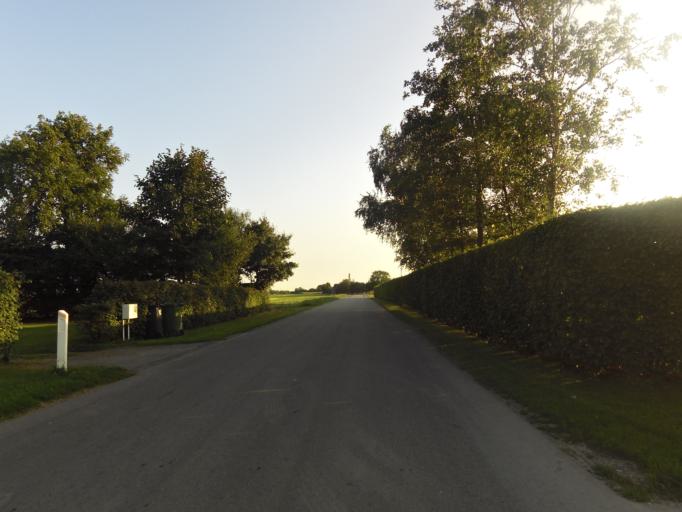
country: DK
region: South Denmark
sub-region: Vejen Kommune
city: Rodding
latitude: 55.3560
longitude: 9.1271
